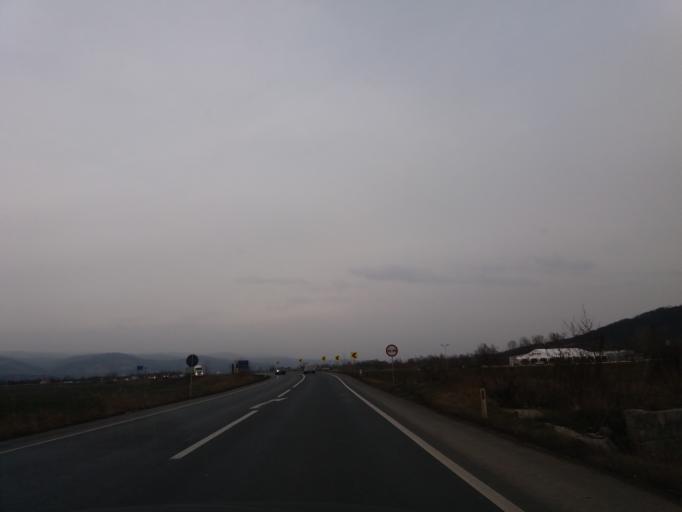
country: RO
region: Hunedoara
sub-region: Oras Simeria
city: Simeria
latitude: 45.8290
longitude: 23.0351
